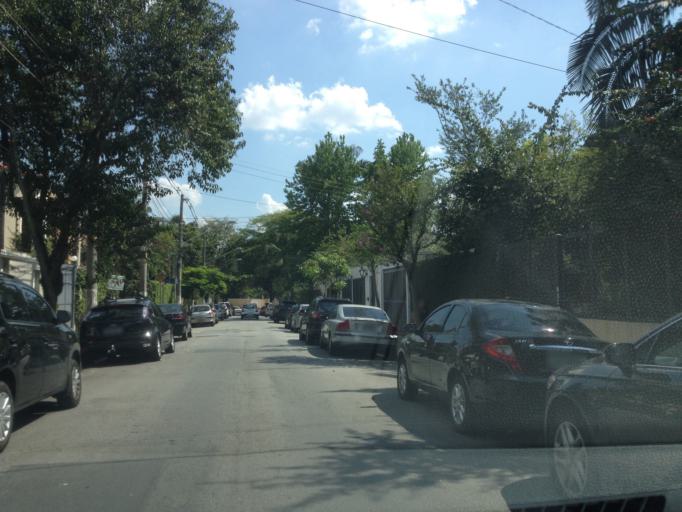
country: BR
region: Sao Paulo
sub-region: Sao Paulo
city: Sao Paulo
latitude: -23.5692
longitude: -46.6784
